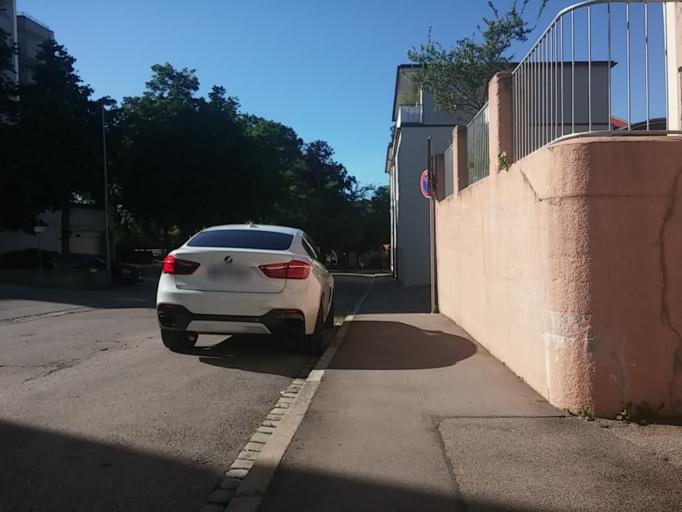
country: DE
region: Bavaria
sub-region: Swabia
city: Kempten (Allgaeu)
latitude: 47.7210
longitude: 10.3129
